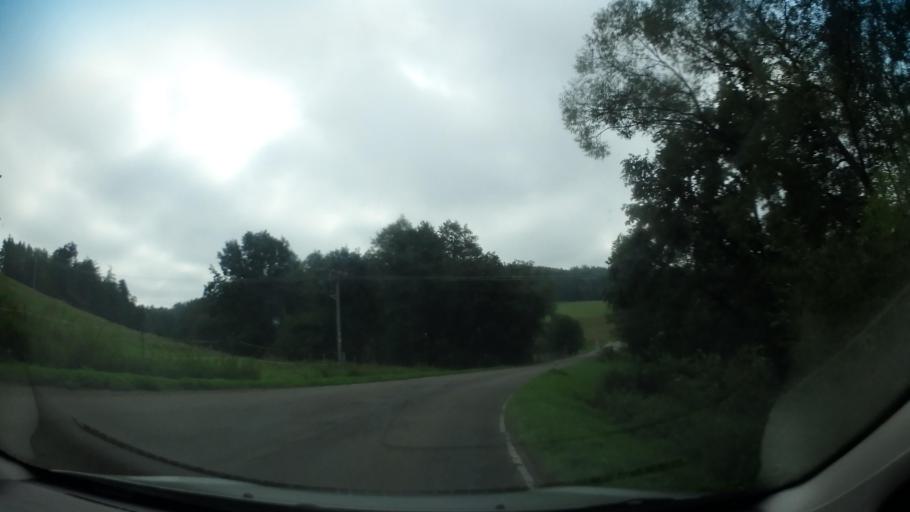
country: CZ
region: Central Bohemia
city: Neveklov
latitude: 49.7318
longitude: 14.4897
